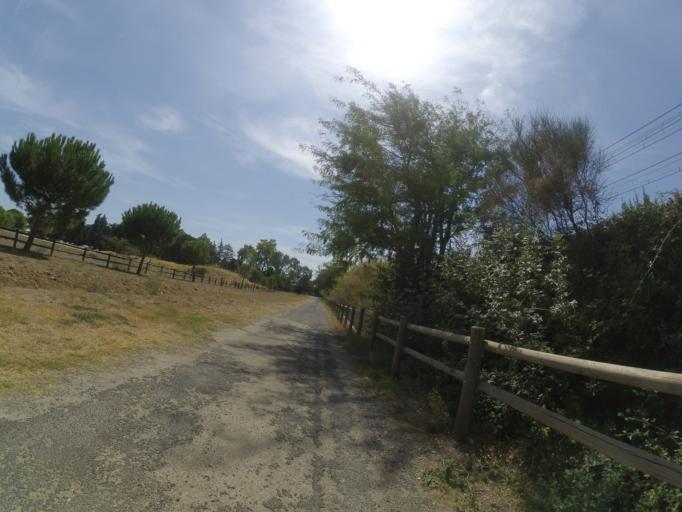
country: FR
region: Languedoc-Roussillon
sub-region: Departement des Pyrenees-Orientales
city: Rivesaltes
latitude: 42.7604
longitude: 2.8707
